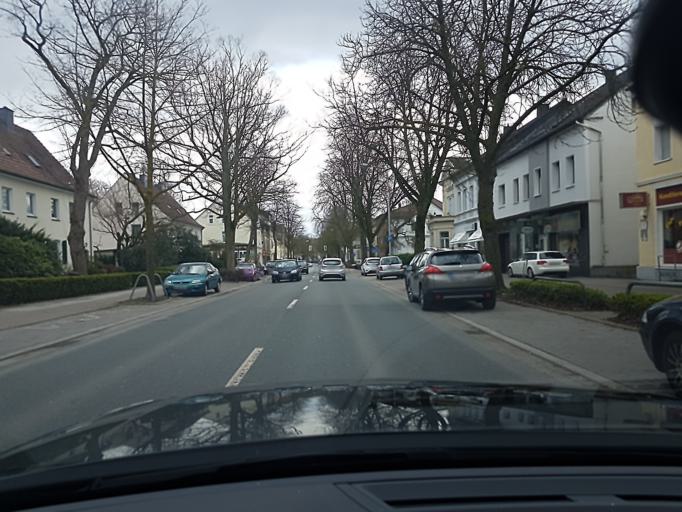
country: DE
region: North Rhine-Westphalia
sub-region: Regierungsbezirk Arnsberg
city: Unna
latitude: 51.5498
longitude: 7.6821
